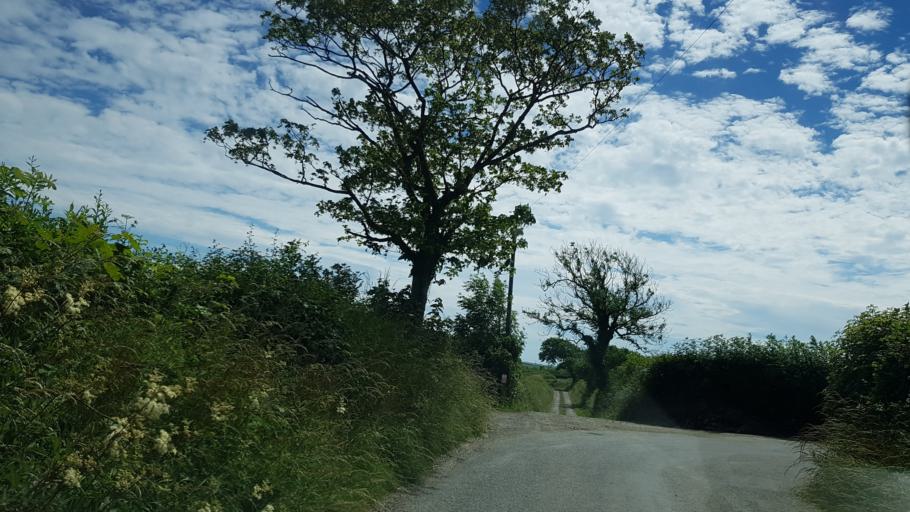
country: GB
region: Wales
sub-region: Pembrokeshire
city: Wiston
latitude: 51.8242
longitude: -4.9104
